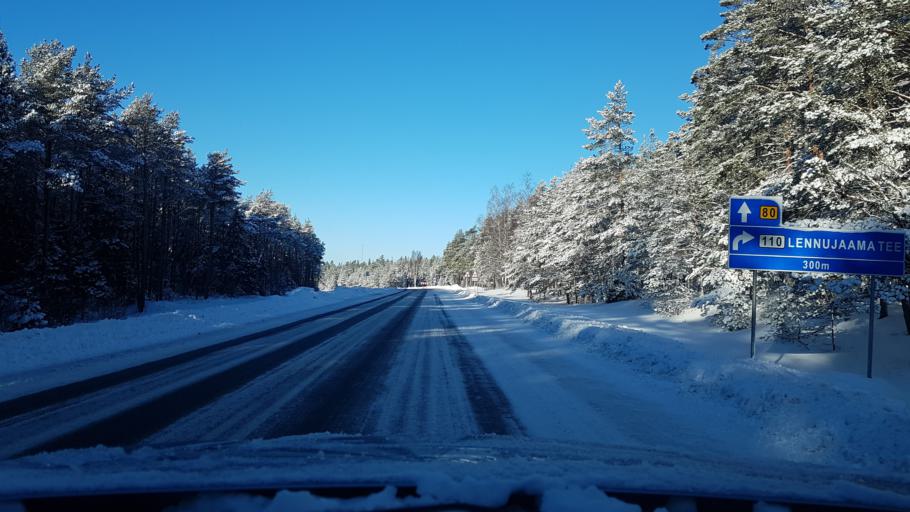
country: EE
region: Hiiumaa
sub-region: Kaerdla linn
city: Kardla
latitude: 58.9882
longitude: 22.7922
